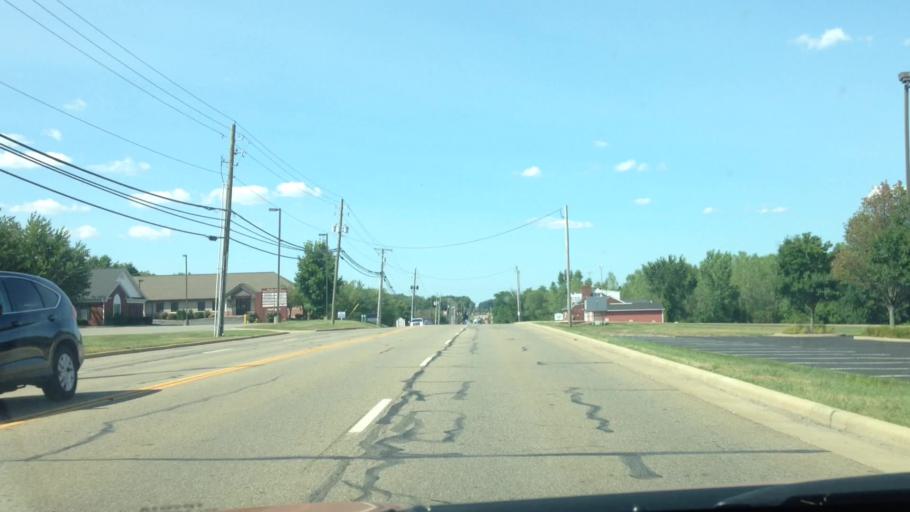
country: US
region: Ohio
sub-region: Stark County
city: North Canton
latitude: 40.8736
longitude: -81.4415
